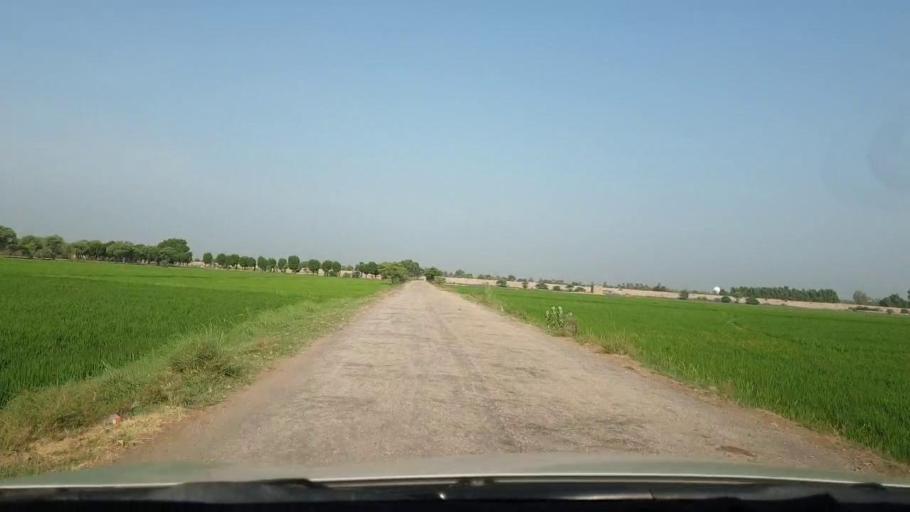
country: PK
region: Sindh
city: Larkana
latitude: 27.5454
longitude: 68.2611
